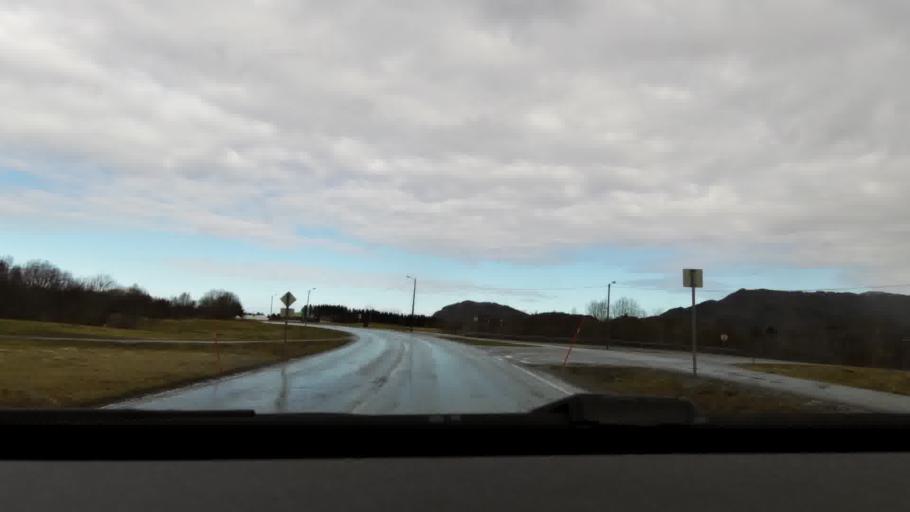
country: NO
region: More og Romsdal
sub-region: Eide
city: Eide
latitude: 62.9610
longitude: 7.3600
